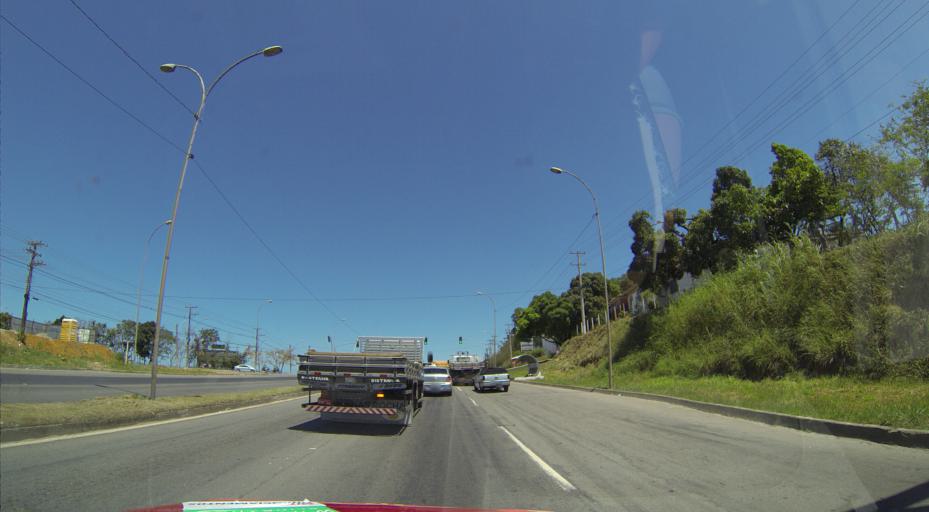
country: BR
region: Espirito Santo
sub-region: Serra
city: Serra
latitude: -20.1728
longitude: -40.2676
